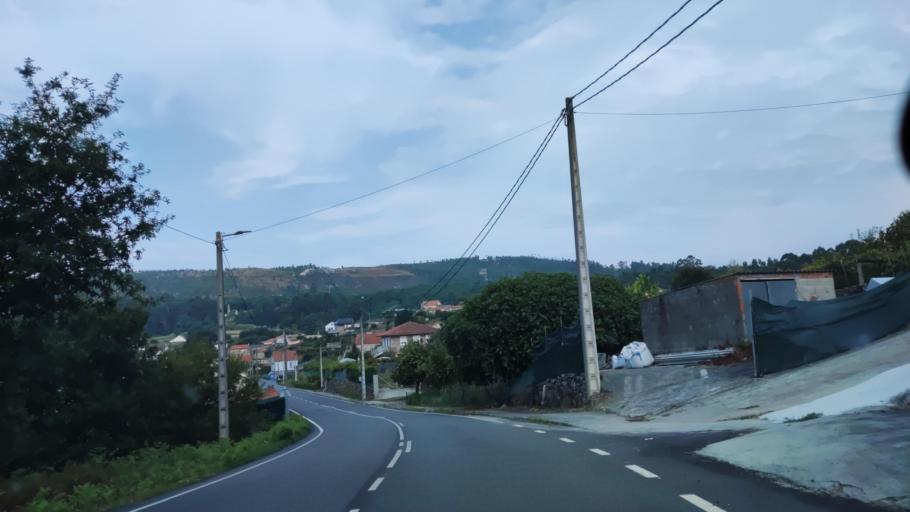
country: ES
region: Galicia
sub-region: Provincia de Pontevedra
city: Catoira
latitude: 42.6534
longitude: -8.7667
